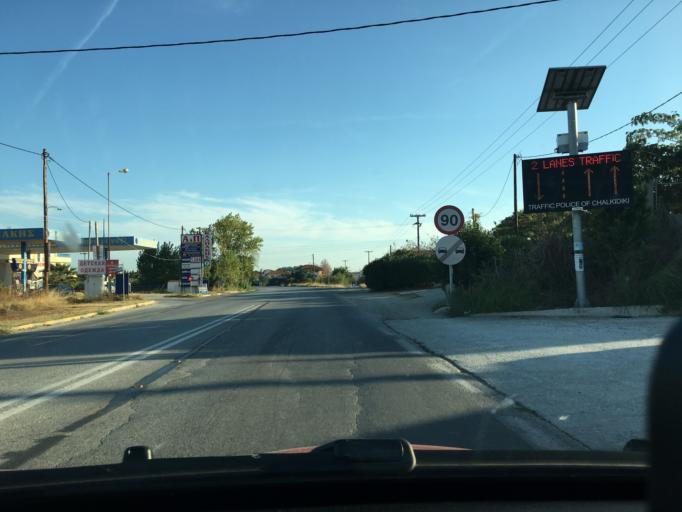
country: GR
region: Central Macedonia
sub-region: Nomos Chalkidikis
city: Nea Potidhaia
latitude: 40.2064
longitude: 23.3233
